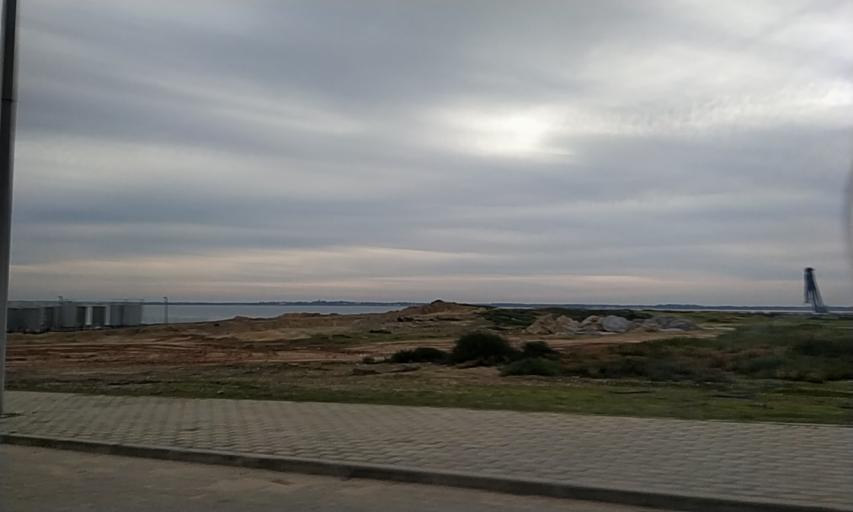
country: PT
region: Setubal
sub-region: Setubal
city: Setubal
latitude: 38.5020
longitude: -8.8384
